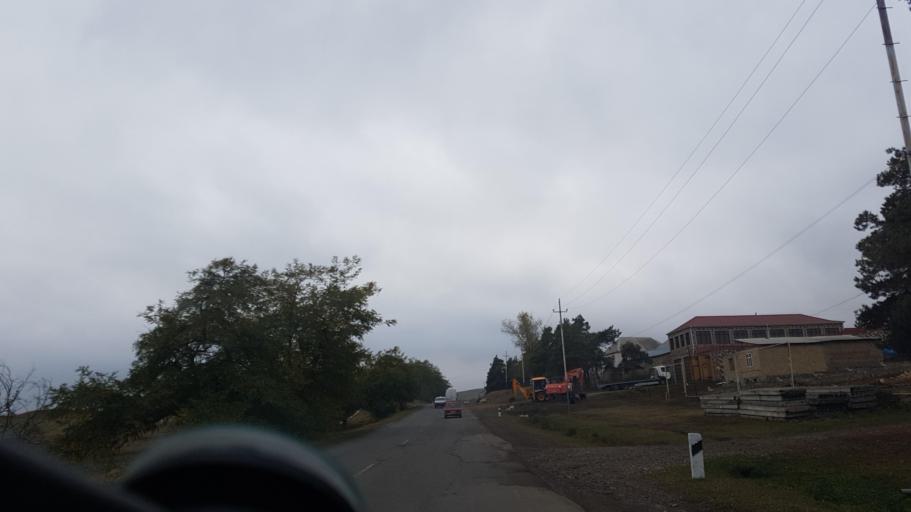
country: AZ
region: Gadabay Rayon
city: Ariqdam
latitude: 40.6410
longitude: 45.8128
